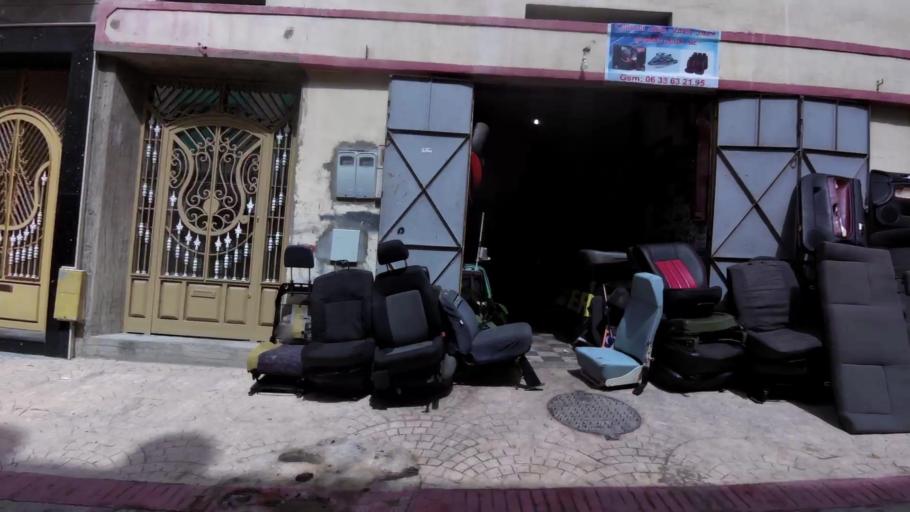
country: MA
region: Tanger-Tetouan
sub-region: Tanger-Assilah
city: Tangier
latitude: 35.7568
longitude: -5.8167
